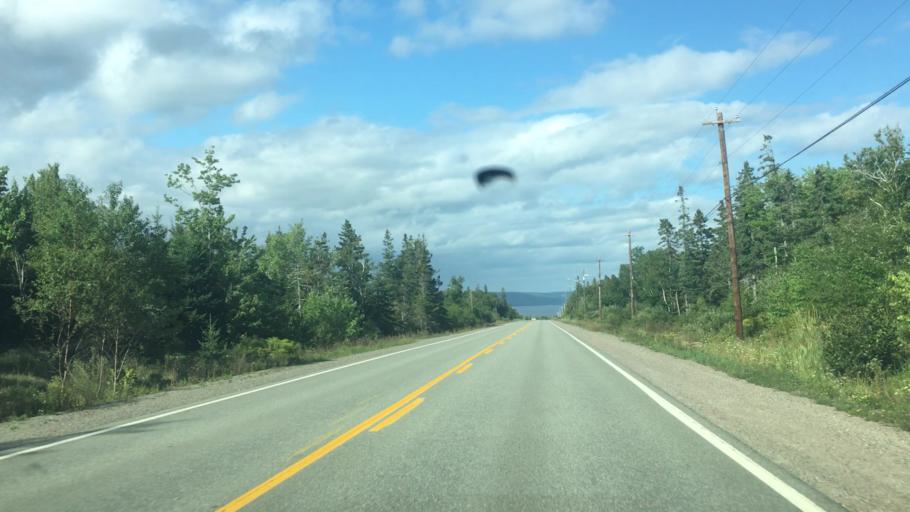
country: CA
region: Nova Scotia
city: Sydney
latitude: 45.8577
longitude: -60.6287
